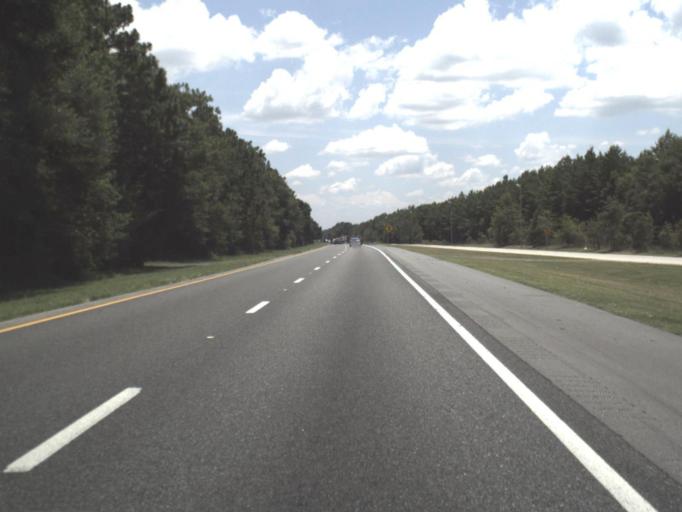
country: US
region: Florida
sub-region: Madison County
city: Madison
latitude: 30.3729
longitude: -83.2680
